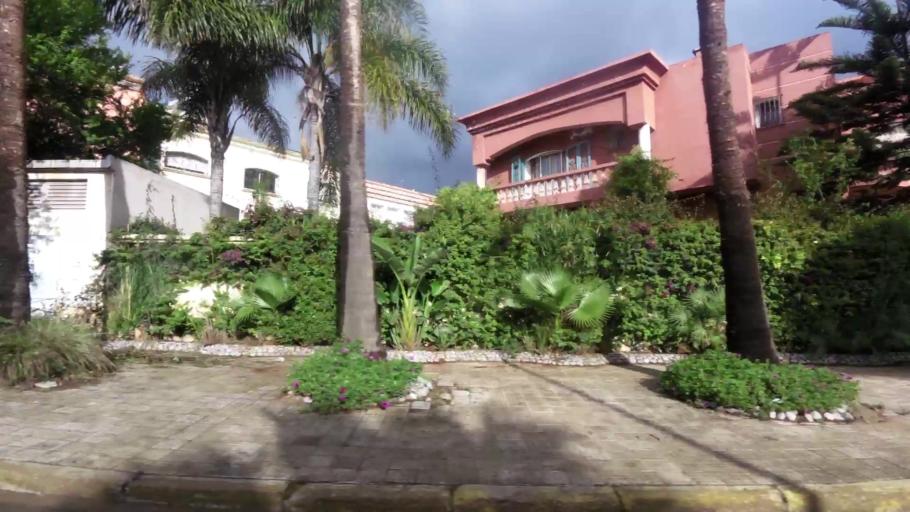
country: MA
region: Grand Casablanca
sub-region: Casablanca
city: Casablanca
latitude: 33.5466
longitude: -7.6612
